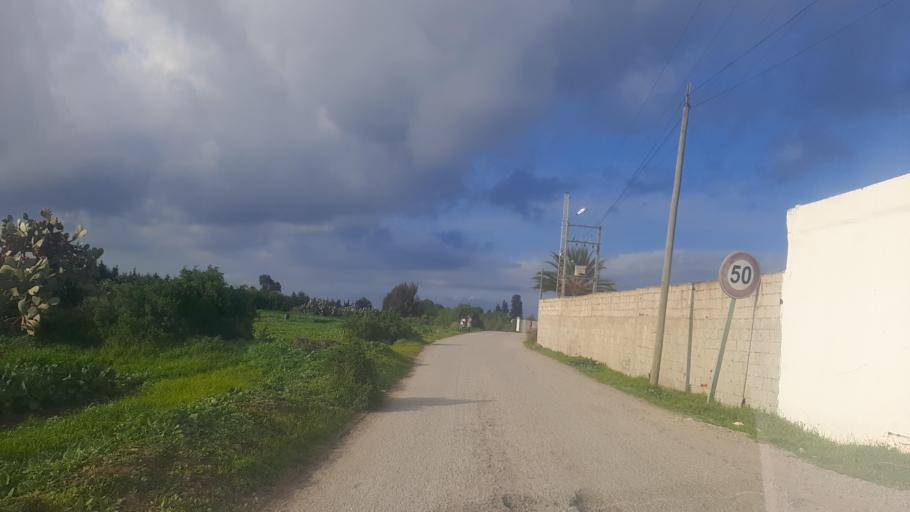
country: TN
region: Nabul
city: Manzil Bu Zalafah
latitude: 36.7081
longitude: 10.5023
